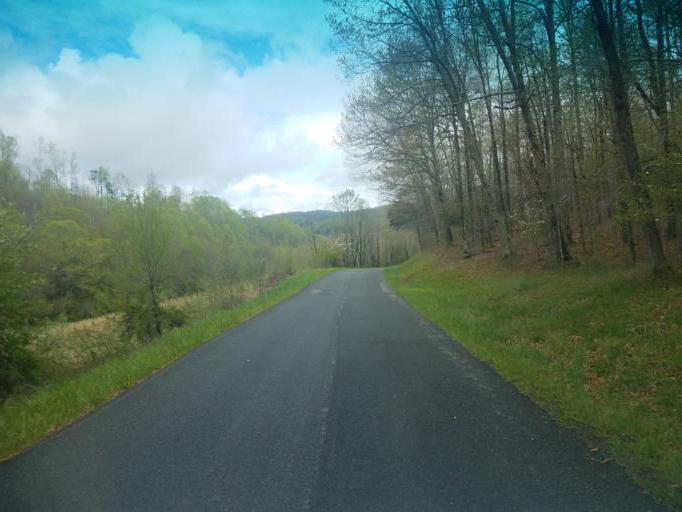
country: US
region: Virginia
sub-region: Smyth County
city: Atkins
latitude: 36.9707
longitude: -81.3896
